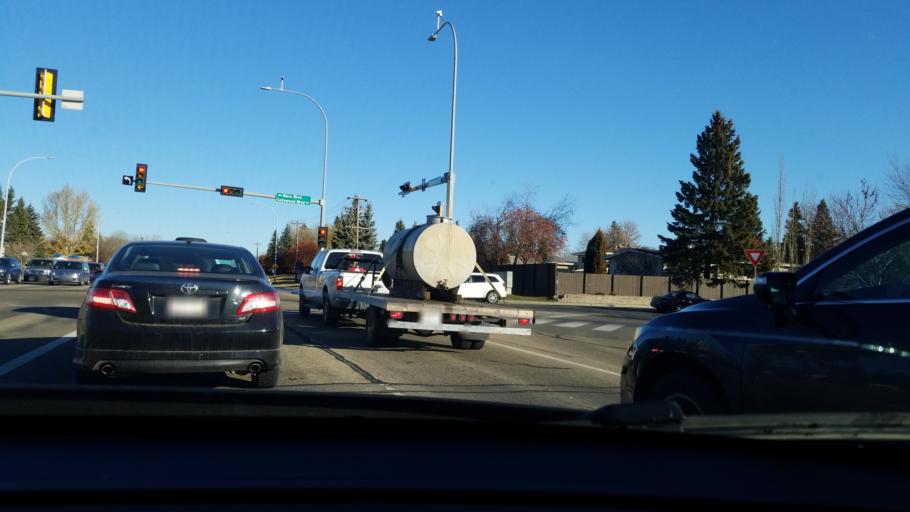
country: CA
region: Alberta
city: Sherwood Park
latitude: 53.5337
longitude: -113.2956
